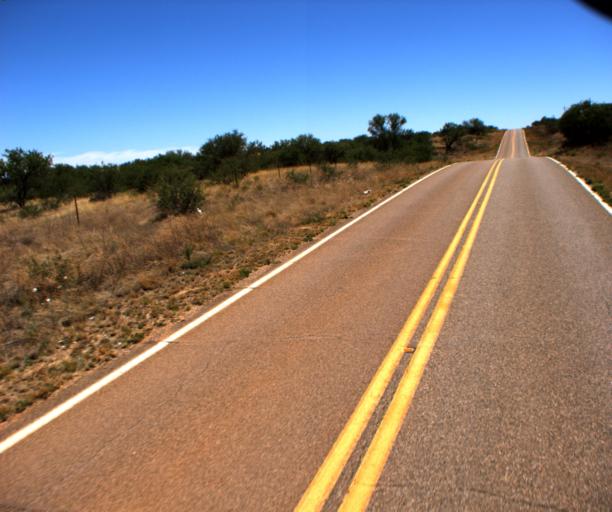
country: US
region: Arizona
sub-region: Pima County
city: Arivaca Junction
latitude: 31.6153
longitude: -111.5166
